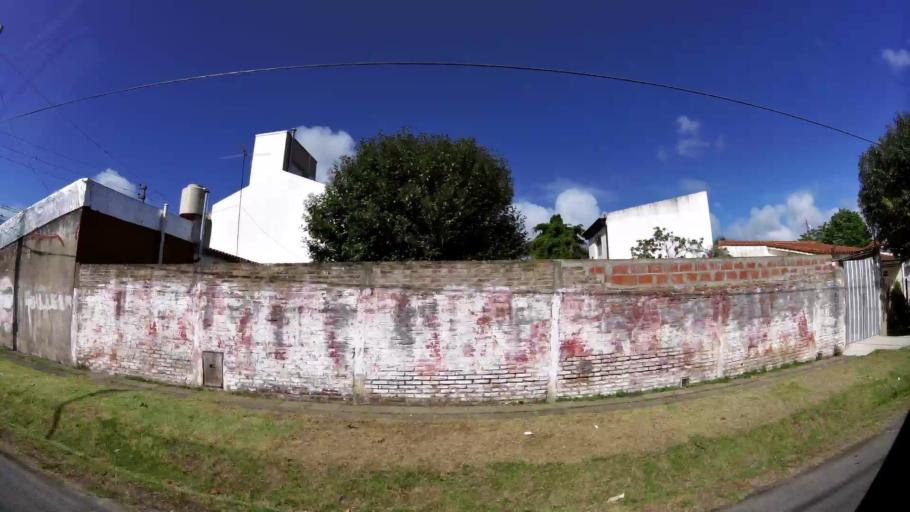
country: AR
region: Buenos Aires
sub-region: Partido de Quilmes
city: Quilmes
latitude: -34.7879
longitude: -58.1530
